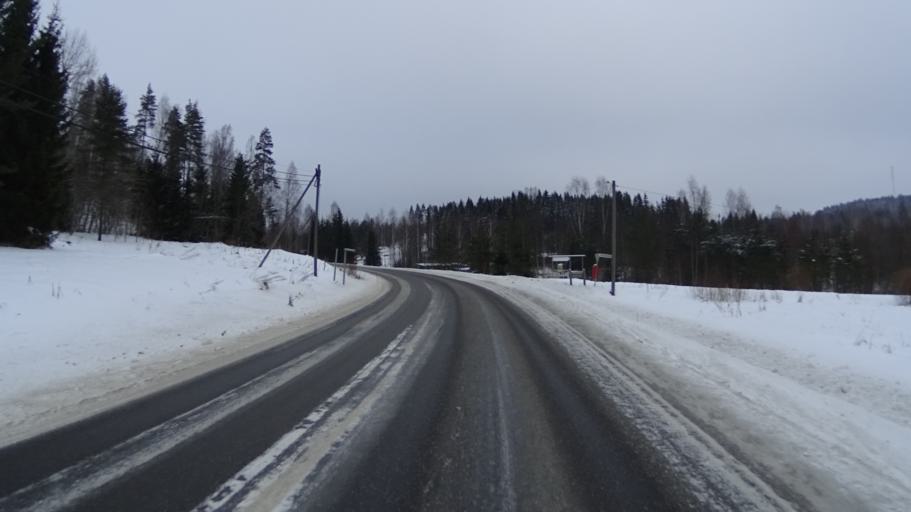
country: FI
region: Uusimaa
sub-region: Helsinki
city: Karkkila
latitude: 60.4966
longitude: 24.1379
